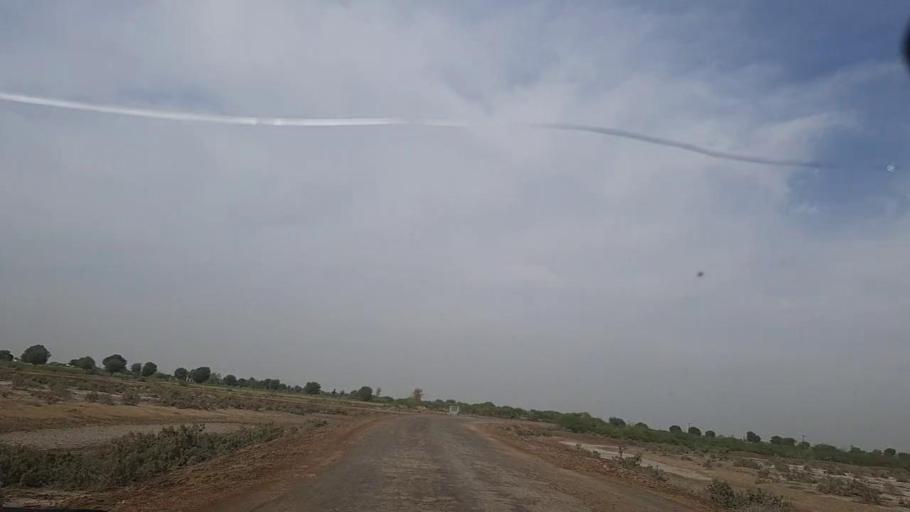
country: PK
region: Sindh
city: Pithoro
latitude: 25.5465
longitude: 69.3607
